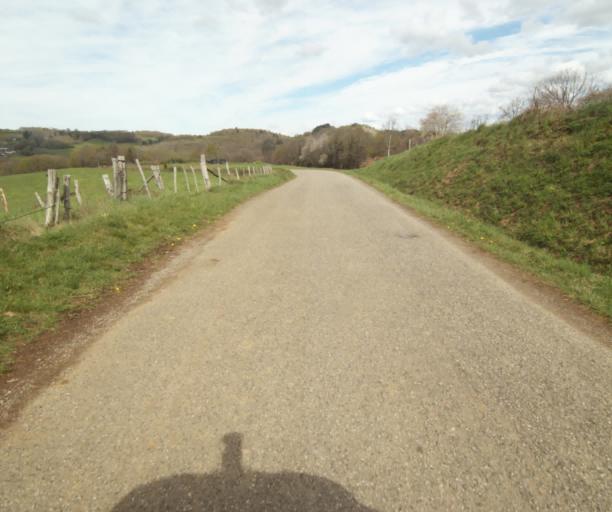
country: FR
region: Limousin
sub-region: Departement de la Correze
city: Laguenne
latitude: 45.2494
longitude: 1.8327
